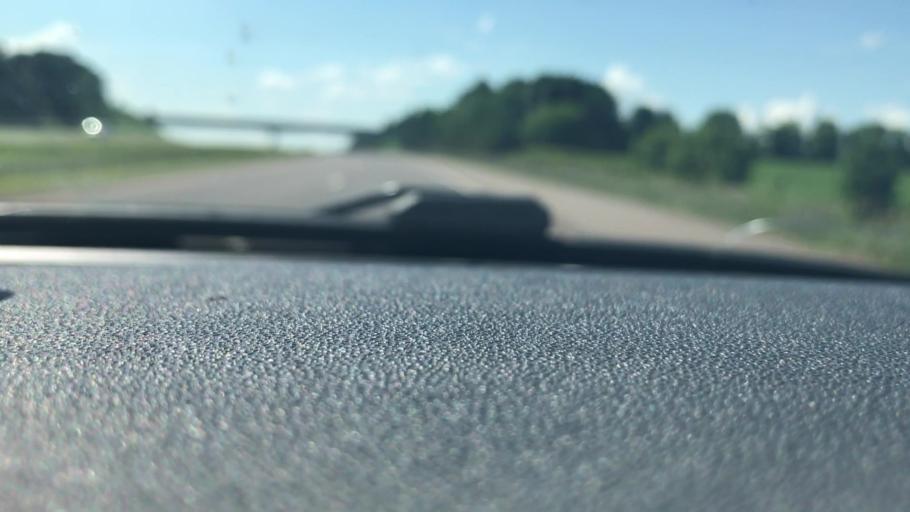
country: US
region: Wisconsin
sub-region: Chippewa County
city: Bloomer
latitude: 45.1211
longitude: -91.5210
